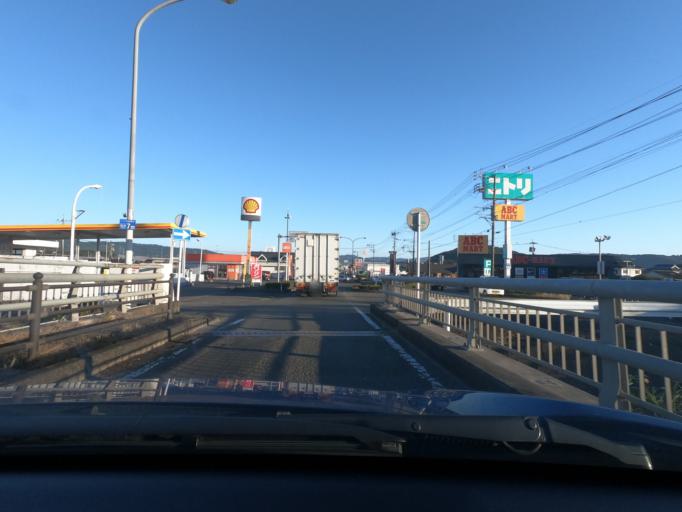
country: JP
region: Kagoshima
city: Satsumasendai
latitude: 31.8368
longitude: 130.2869
